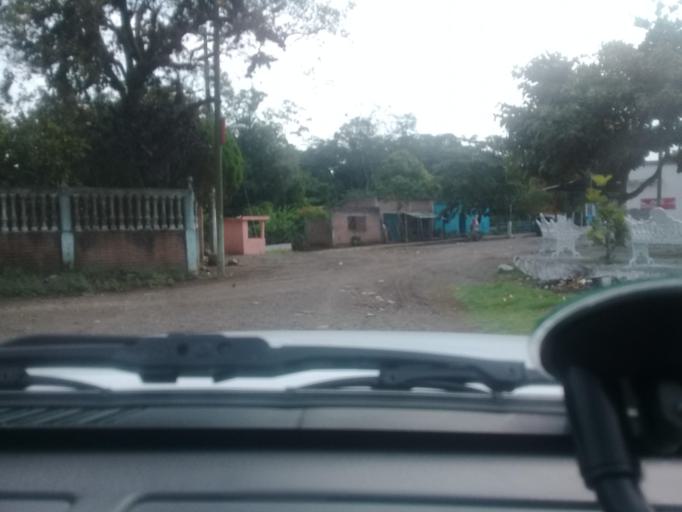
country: MX
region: Veracruz
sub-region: Paso de Ovejas
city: Tolome
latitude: 19.2626
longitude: -96.4125
